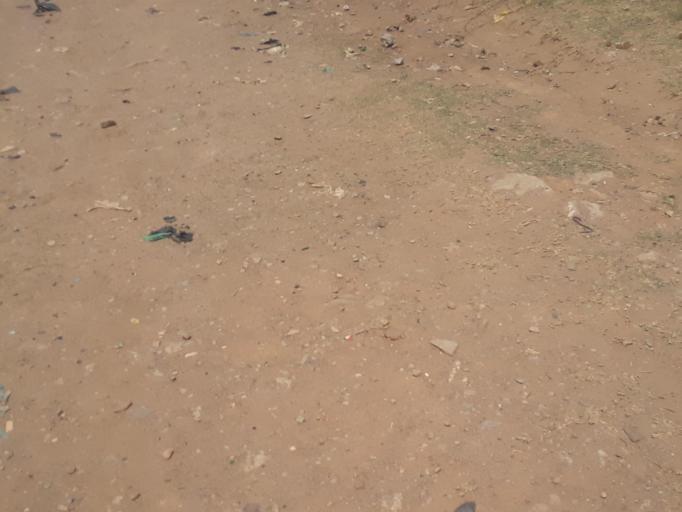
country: ZM
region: Lusaka
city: Lusaka
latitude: -15.3684
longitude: 28.2893
